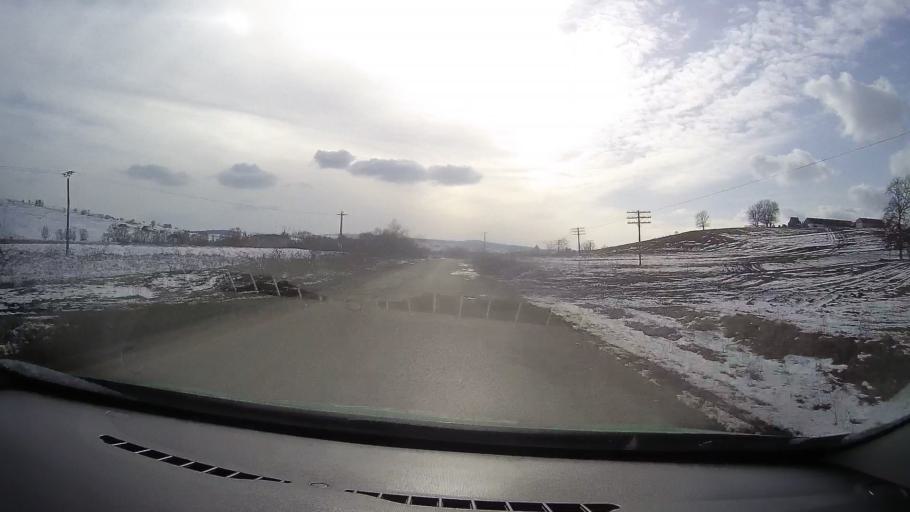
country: RO
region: Sibiu
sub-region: Comuna Bradeni
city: Bradeni
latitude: 46.0664
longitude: 24.7991
